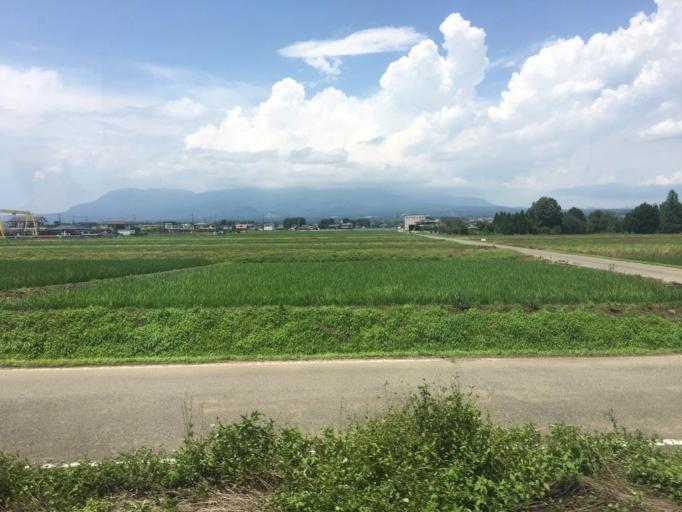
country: JP
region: Gunma
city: Omamacho-omama
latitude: 36.4178
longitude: 139.2150
